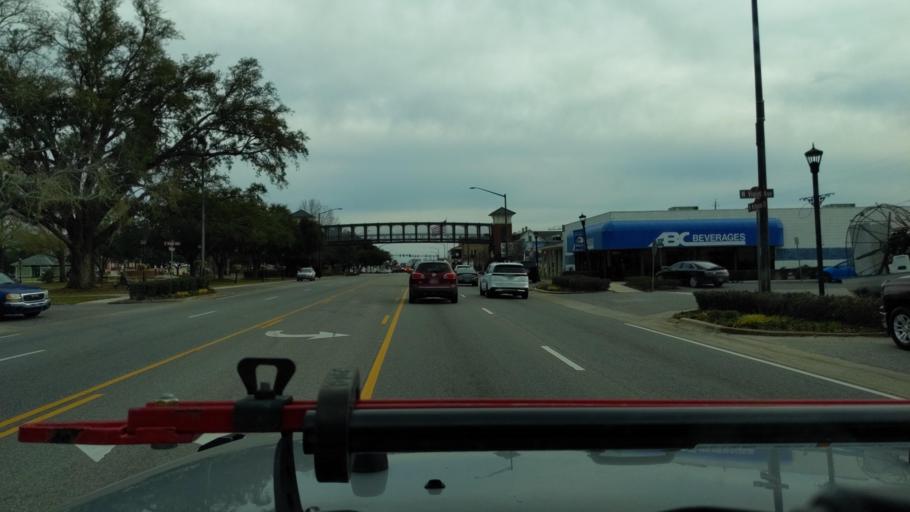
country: US
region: Alabama
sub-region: Baldwin County
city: Foley
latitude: 30.4089
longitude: -87.6838
